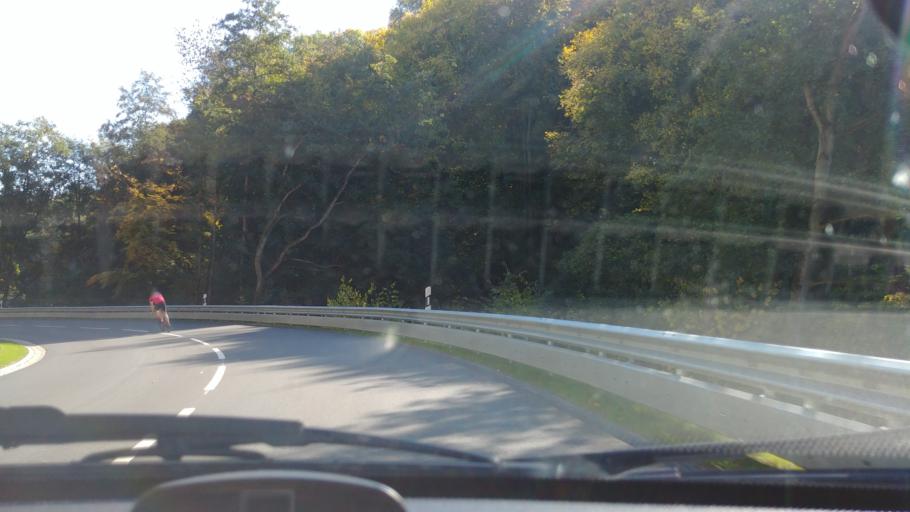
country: DE
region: Rheinland-Pfalz
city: Mudershausen
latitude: 50.2862
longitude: 8.0484
